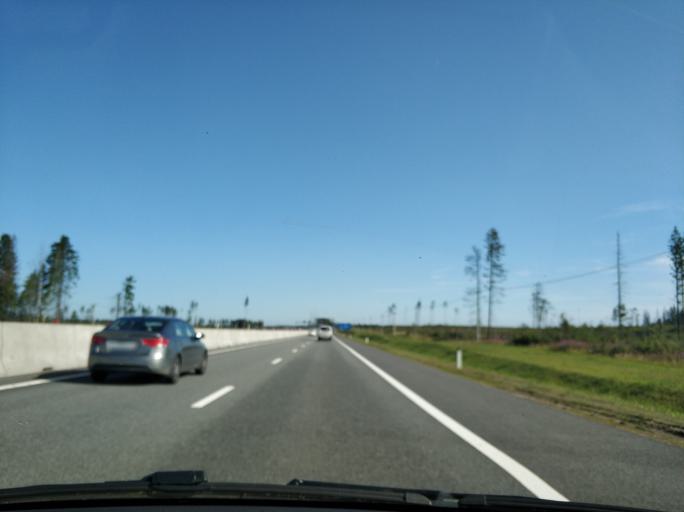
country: RU
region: Leningrad
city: Sosnovo
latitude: 60.4942
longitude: 30.1959
